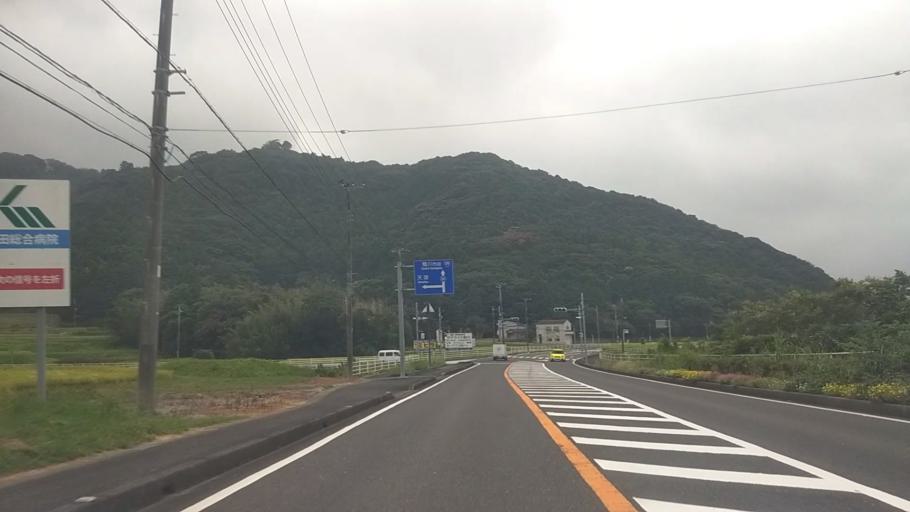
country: JP
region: Chiba
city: Kawaguchi
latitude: 35.1333
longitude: 140.0780
